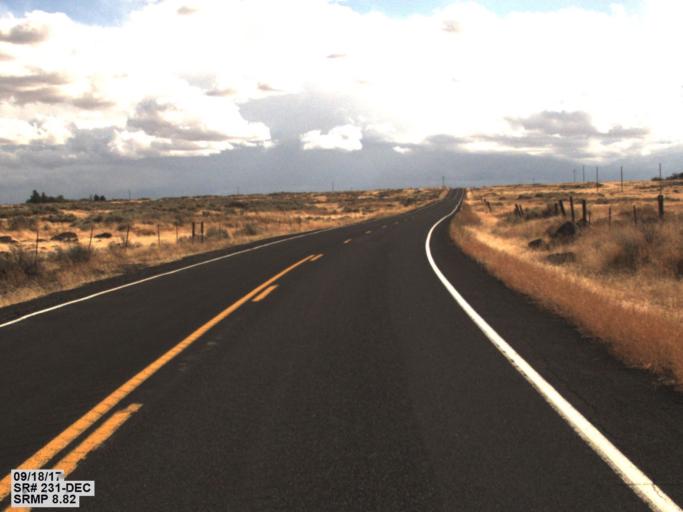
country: US
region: Washington
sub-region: Spokane County
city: Medical Lake
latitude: 47.4292
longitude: -117.9047
